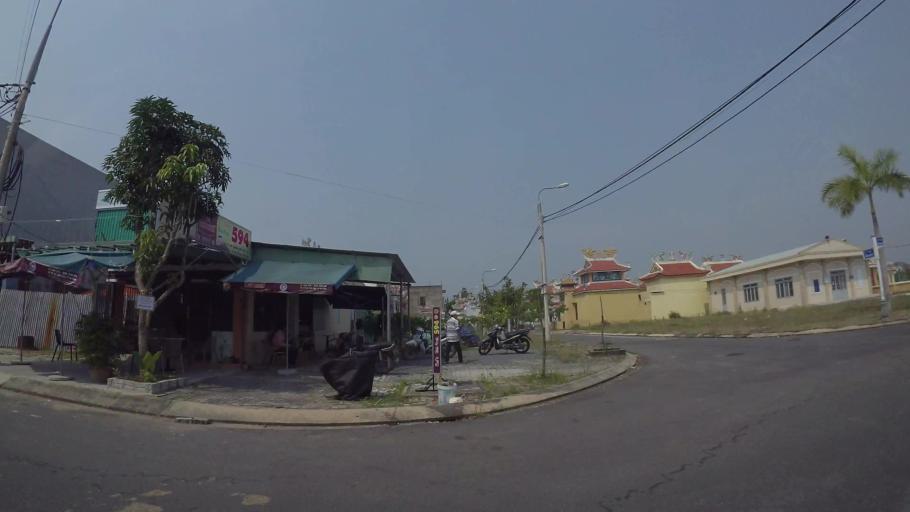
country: VN
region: Da Nang
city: Cam Le
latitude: 15.9762
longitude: 108.2144
